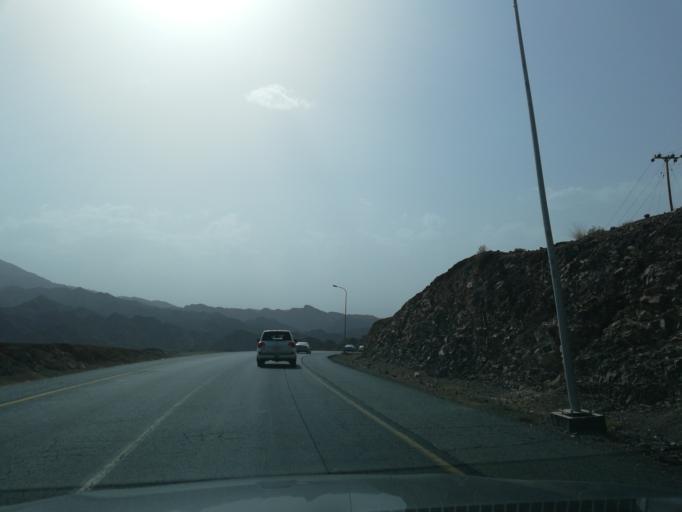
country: OM
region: Muhafazat ad Dakhiliyah
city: Sufalat Sama'il
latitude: 23.1863
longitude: 58.0946
